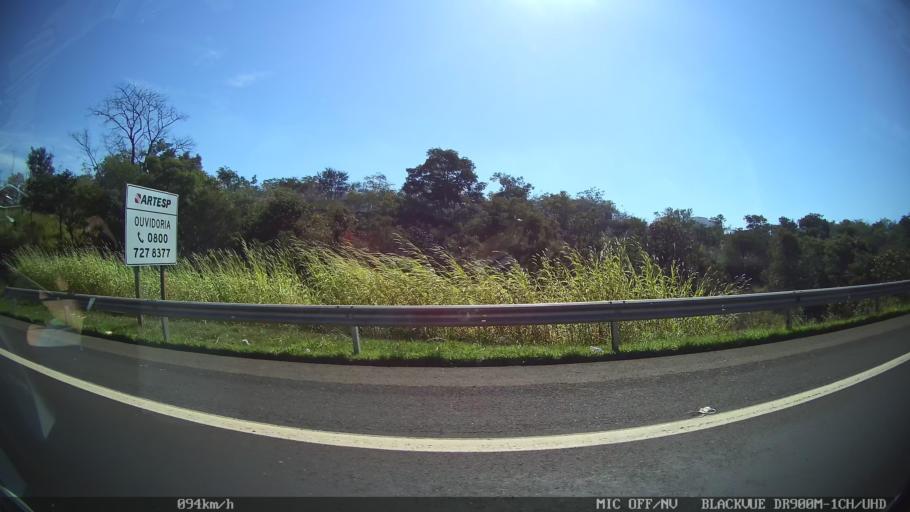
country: BR
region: Sao Paulo
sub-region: Franca
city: Franca
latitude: -20.5558
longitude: -47.4341
